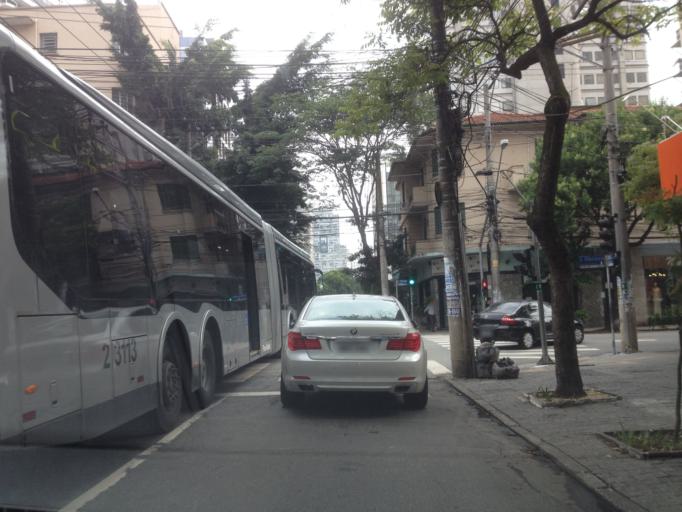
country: BR
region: Sao Paulo
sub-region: Sao Paulo
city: Sao Paulo
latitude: -23.5840
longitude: -46.6736
